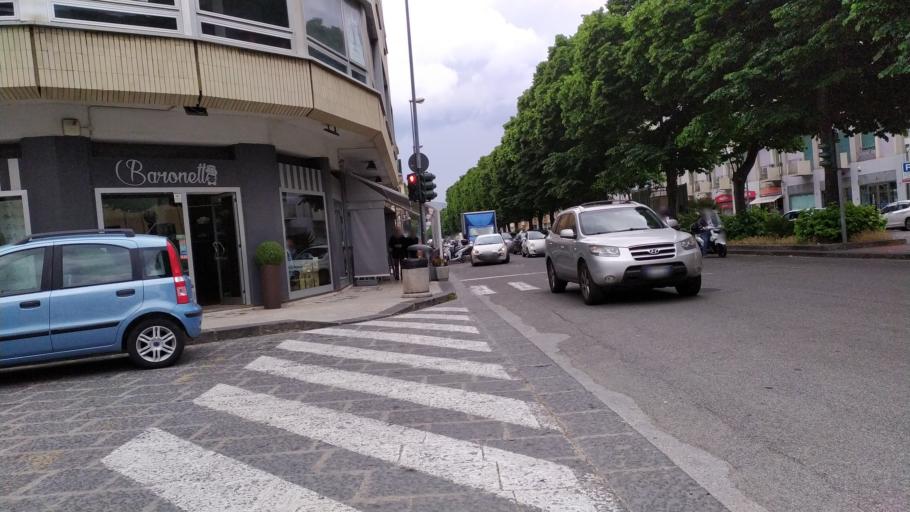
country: IT
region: Sicily
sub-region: Messina
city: Messina
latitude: 38.1901
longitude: 15.5564
